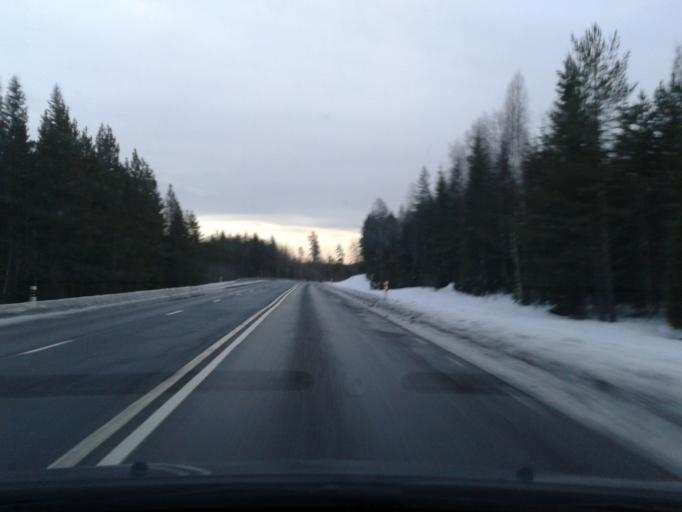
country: SE
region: Vaesternorrland
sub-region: Kramfors Kommun
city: Bollstabruk
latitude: 63.1069
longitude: 17.5067
